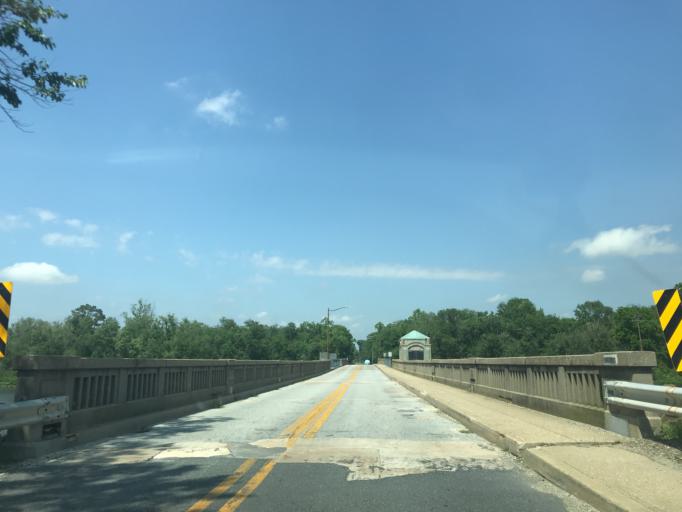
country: US
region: Maryland
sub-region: Dorchester County
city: Hurlock
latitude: 38.5760
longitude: -75.7952
